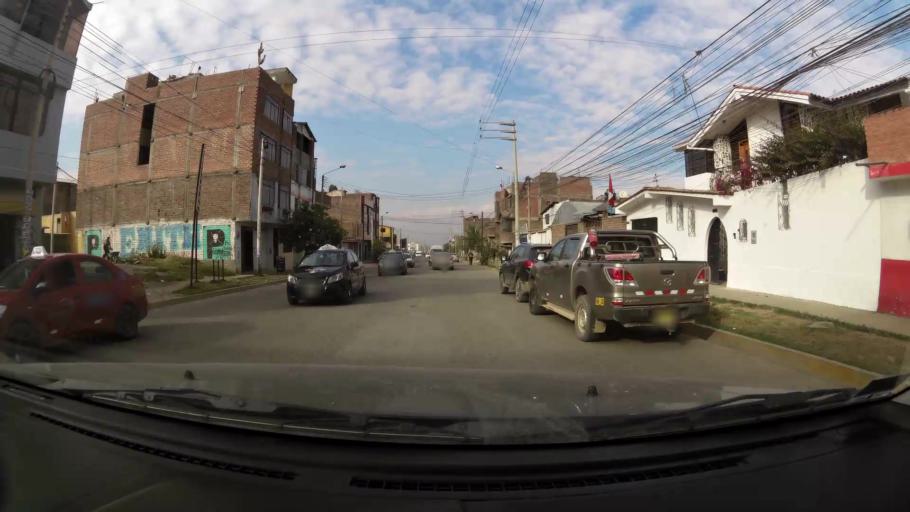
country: PE
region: Junin
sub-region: Provincia de Huancayo
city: Huancayo
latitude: -12.0429
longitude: -75.1936
